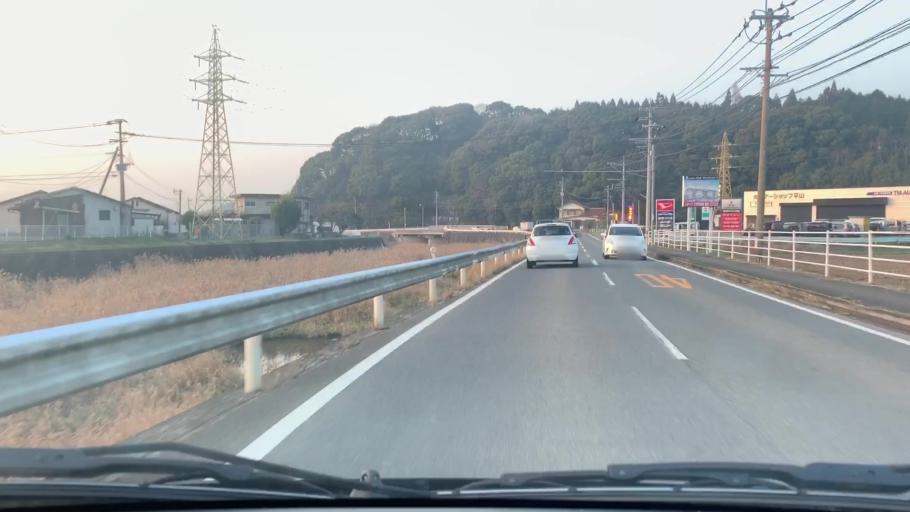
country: JP
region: Saga Prefecture
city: Imaricho-ko
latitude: 33.2703
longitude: 129.8955
